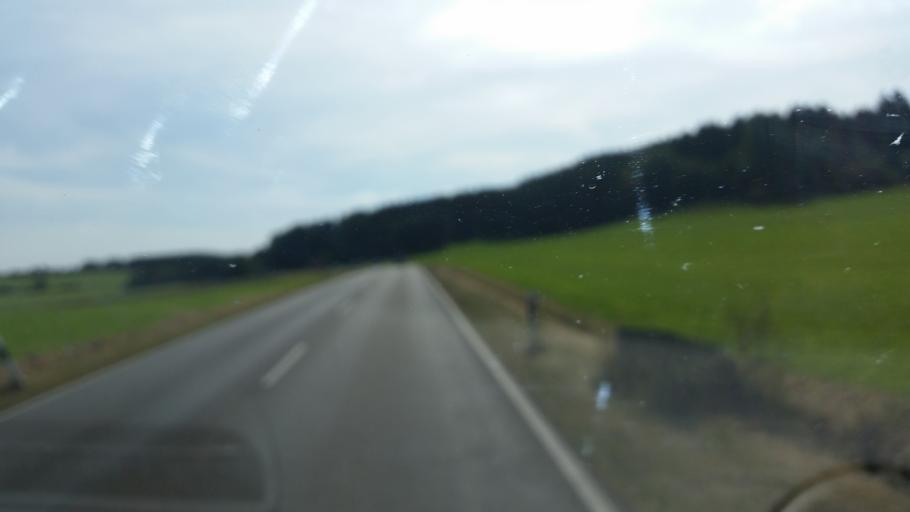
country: DE
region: Rheinland-Pfalz
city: Kaden
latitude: 50.5577
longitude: 7.8927
